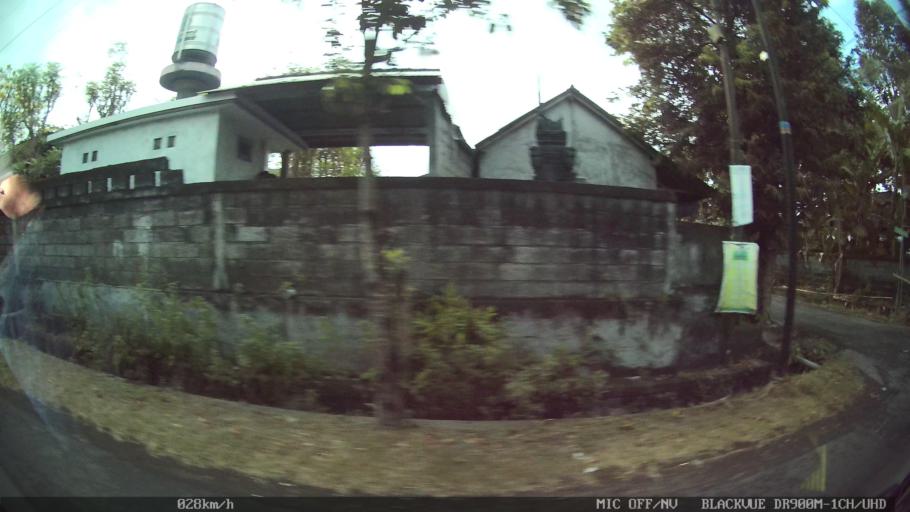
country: ID
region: Bali
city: Banjar Bucu
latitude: -8.5892
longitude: 115.2053
